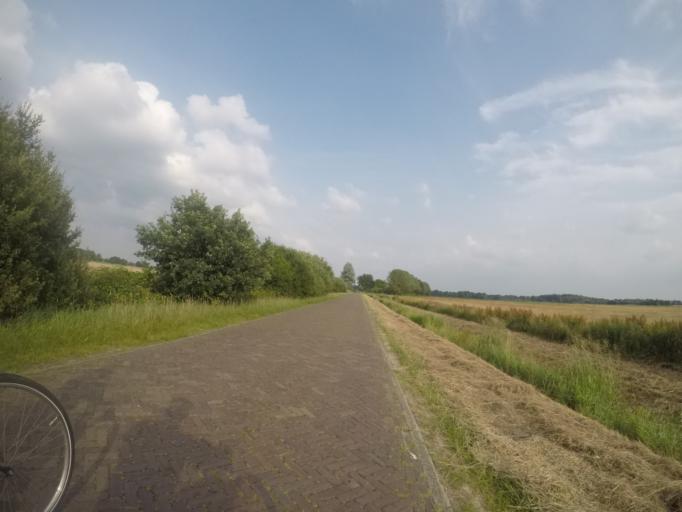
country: NL
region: Friesland
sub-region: Gemeente Weststellingwerf
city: Noordwolde
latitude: 52.8862
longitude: 6.2567
